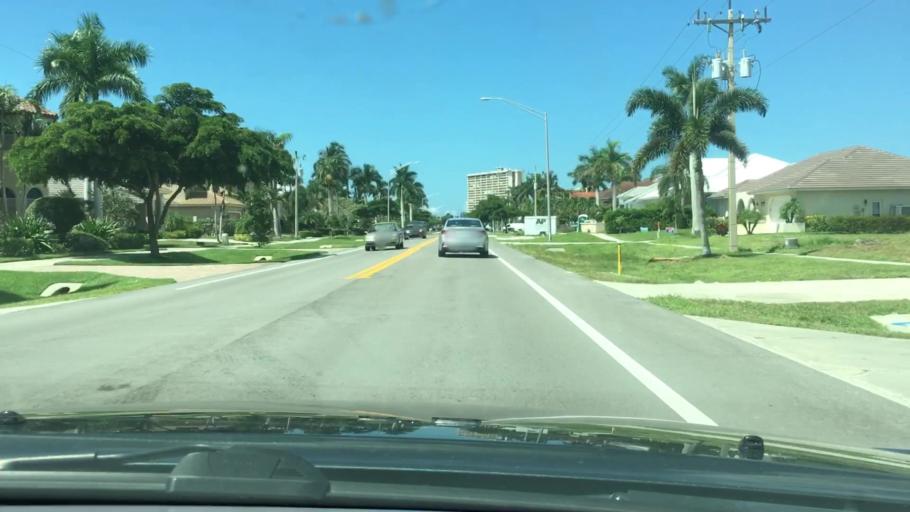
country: US
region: Florida
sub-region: Collier County
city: Marco
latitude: 25.9371
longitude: -81.7236
